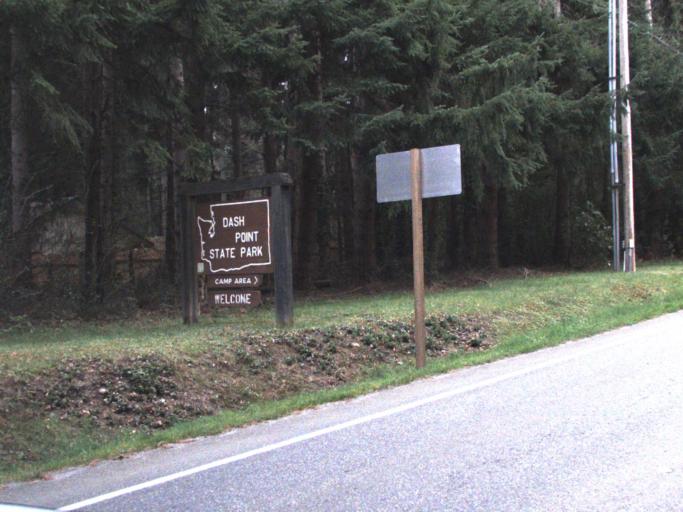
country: US
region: Washington
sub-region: Pierce County
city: Tacoma
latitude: 47.3180
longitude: -122.4065
